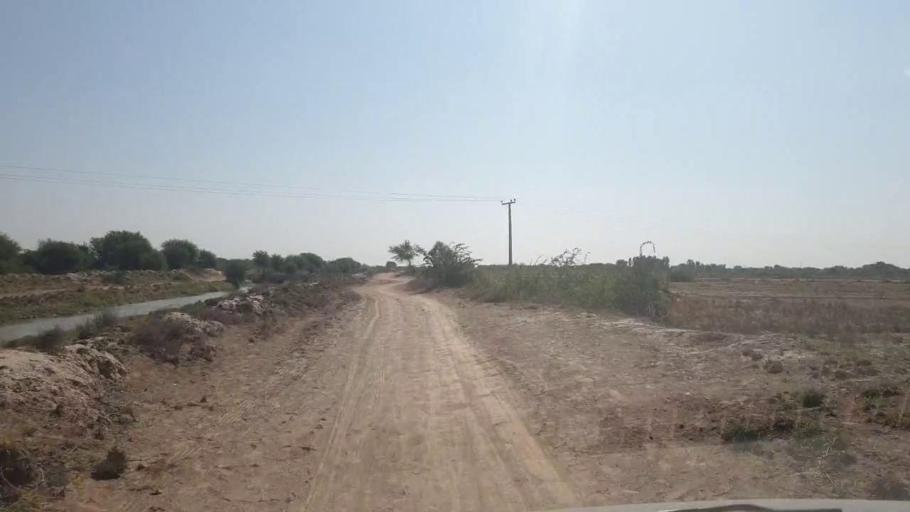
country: PK
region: Sindh
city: Digri
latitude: 24.9337
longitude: 69.1635
